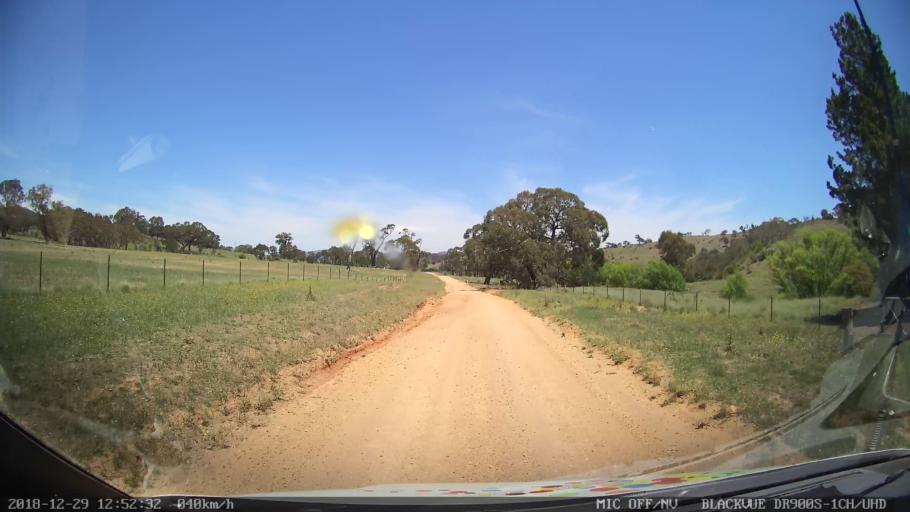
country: AU
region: Australian Capital Territory
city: Macarthur
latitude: -35.6813
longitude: 149.1937
